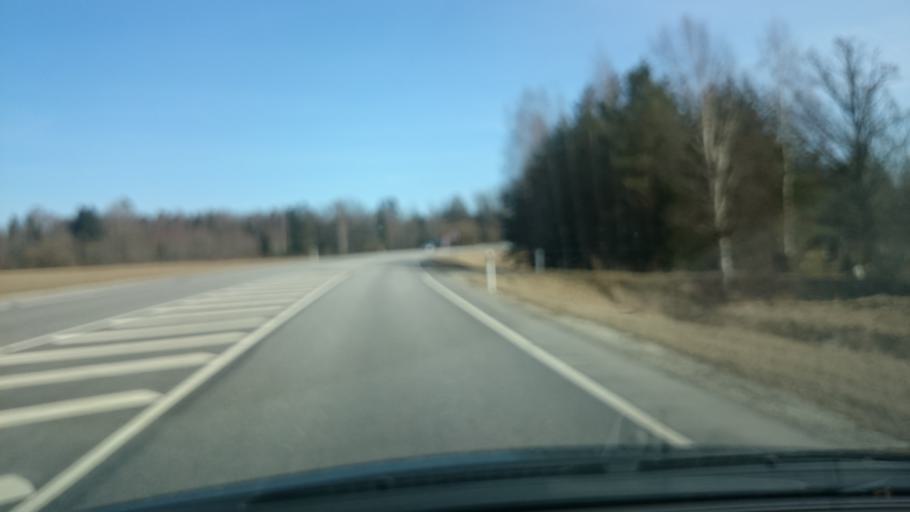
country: EE
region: Paernumaa
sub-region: Vaendra vald (alev)
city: Vandra
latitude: 58.6733
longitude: 25.1161
